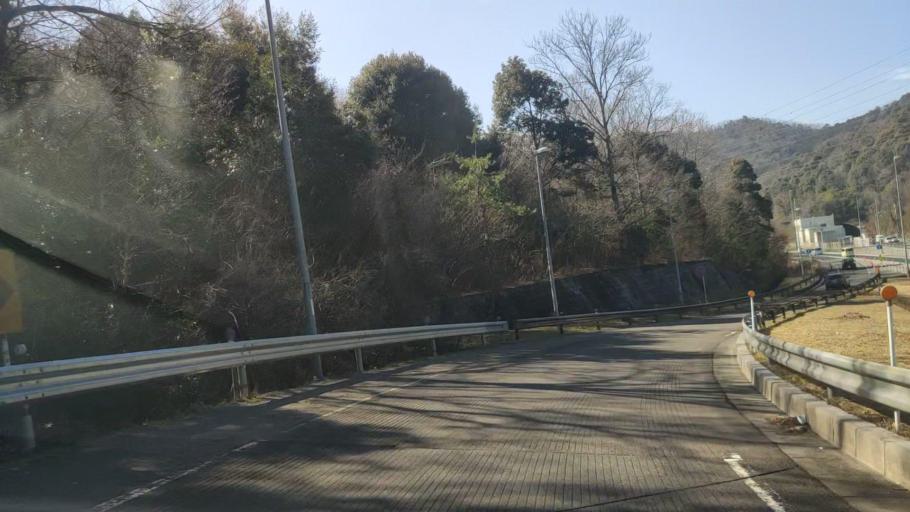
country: JP
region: Gifu
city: Gifu-shi
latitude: 35.4276
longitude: 136.7964
